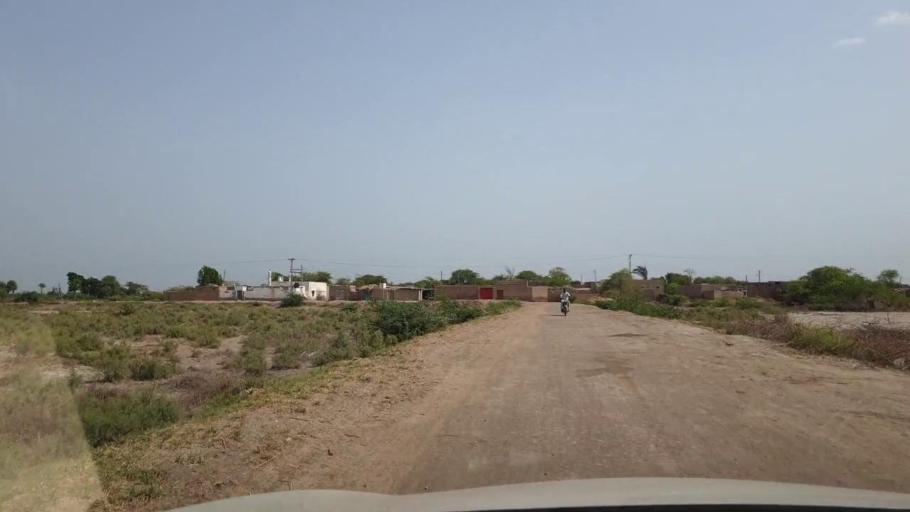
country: PK
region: Sindh
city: Mirwah Gorchani
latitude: 25.2775
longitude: 68.9583
